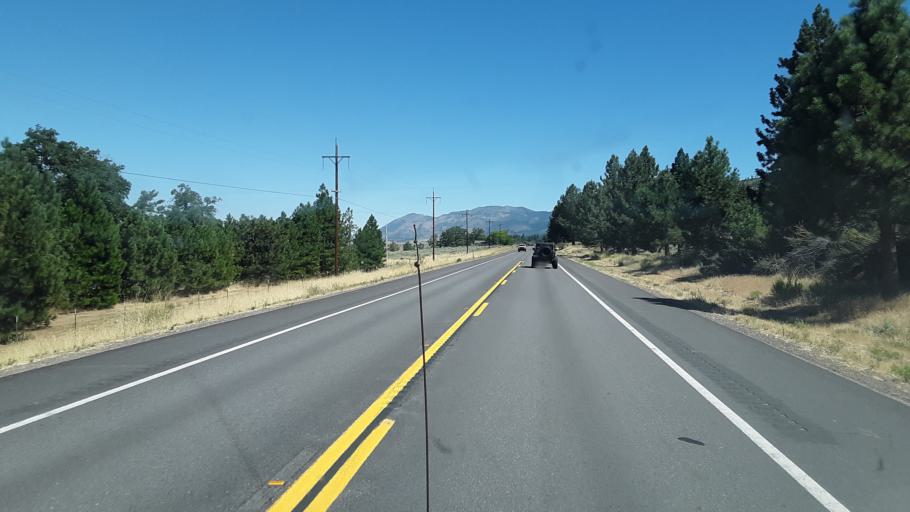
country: US
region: California
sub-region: Lassen County
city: Janesville
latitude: 40.2419
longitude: -120.4539
